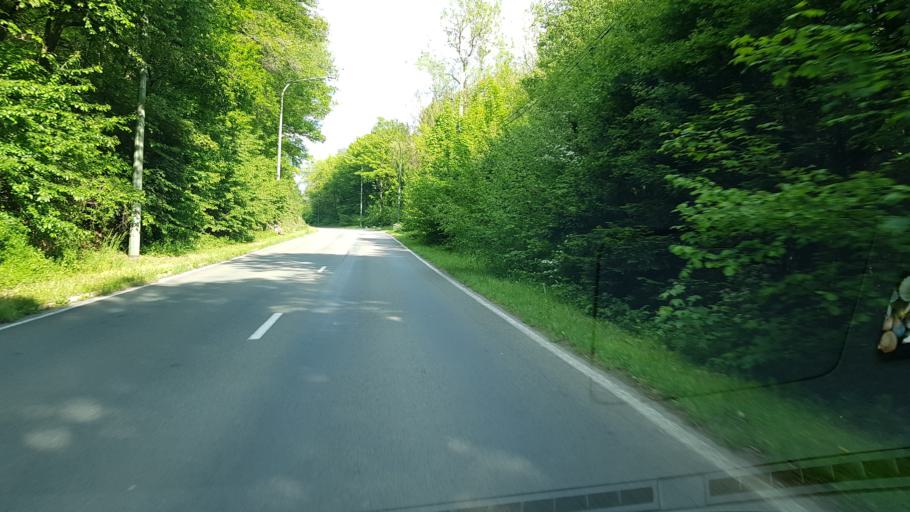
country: BE
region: Wallonia
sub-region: Province de Liege
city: Trooz
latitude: 50.5365
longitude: 5.6946
